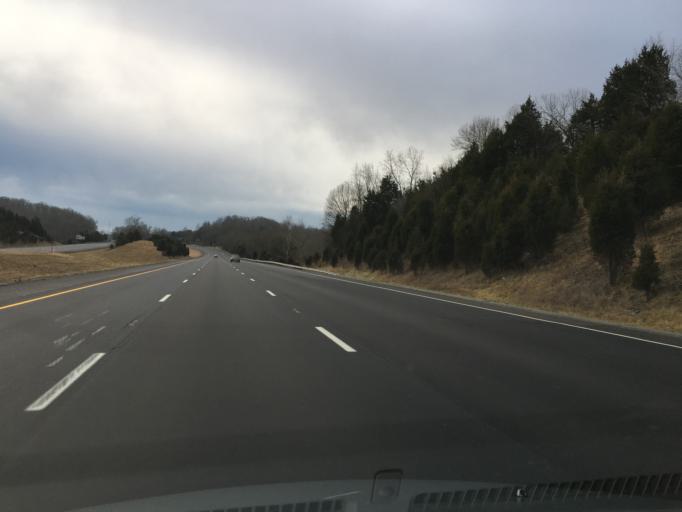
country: US
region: Kentucky
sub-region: Scott County
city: Georgetown
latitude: 38.3750
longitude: -84.5706
